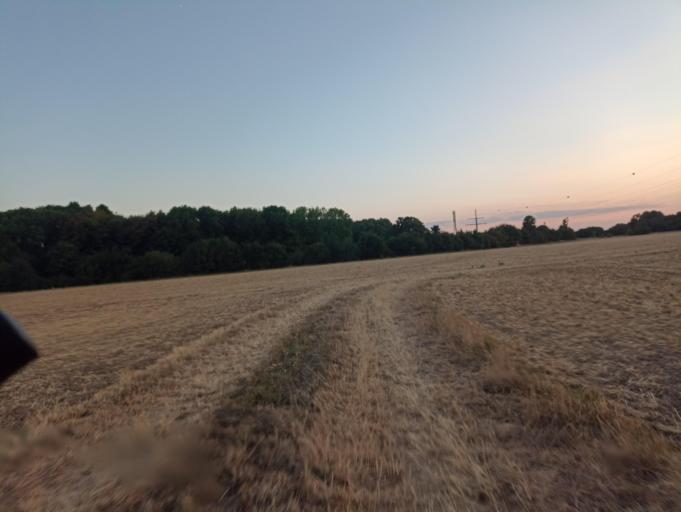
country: DE
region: Hesse
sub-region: Regierungsbezirk Darmstadt
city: Bad Homburg vor der Hoehe
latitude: 50.2032
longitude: 8.6456
